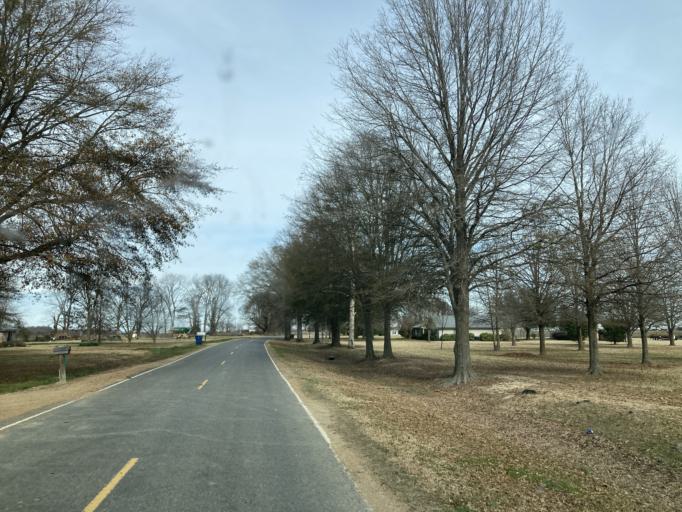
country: US
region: Mississippi
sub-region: Humphreys County
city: Belzoni
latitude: 33.1310
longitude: -90.6112
